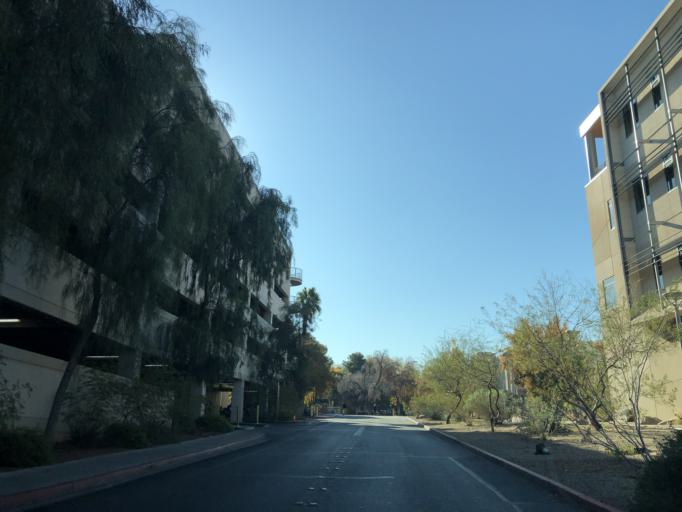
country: US
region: Nevada
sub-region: Clark County
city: Paradise
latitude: 36.1113
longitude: -115.1408
